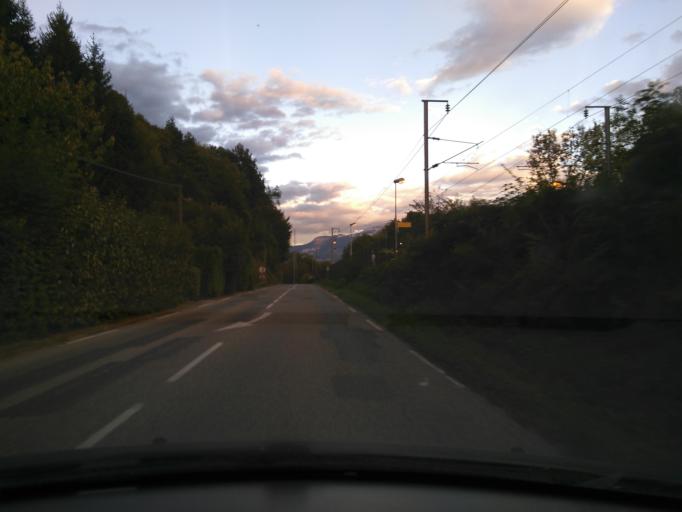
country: FR
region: Rhone-Alpes
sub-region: Departement de l'Isere
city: La Murette
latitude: 45.3690
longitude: 5.5356
